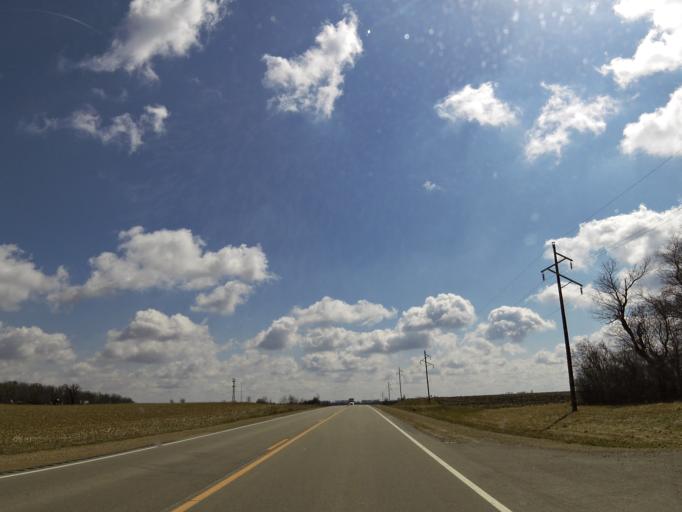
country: US
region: Minnesota
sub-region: Goodhue County
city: Kenyon
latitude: 44.2940
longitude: -92.9798
